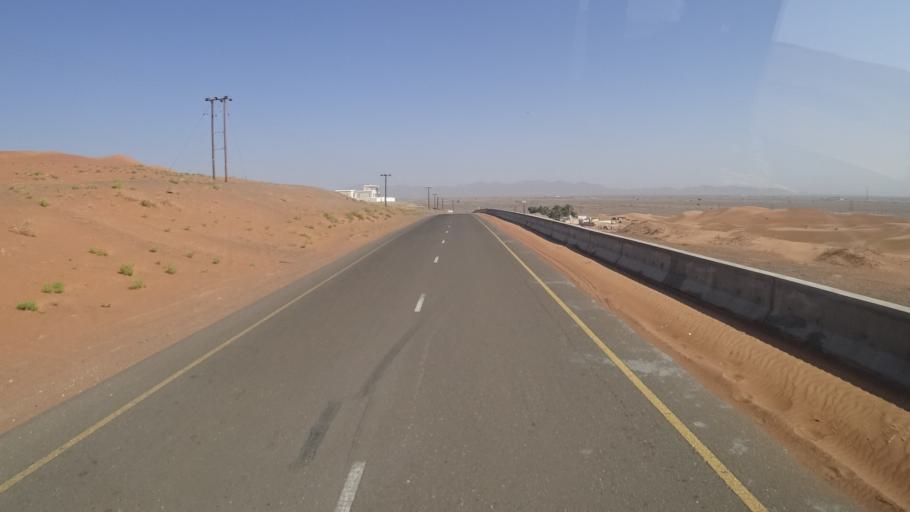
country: OM
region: Ash Sharqiyah
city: Al Qabil
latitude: 22.4966
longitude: 58.7156
